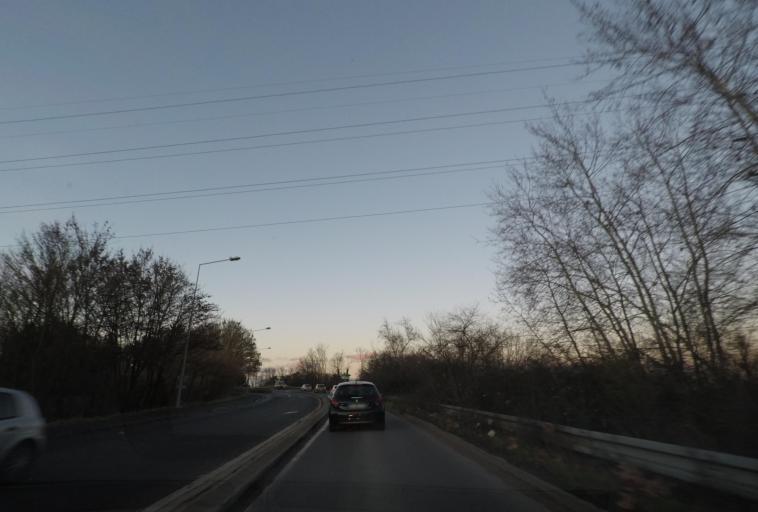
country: FR
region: Ile-de-France
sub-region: Departement de l'Essonne
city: Saint-Michel-sur-Orge
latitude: 48.6237
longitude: 2.3148
